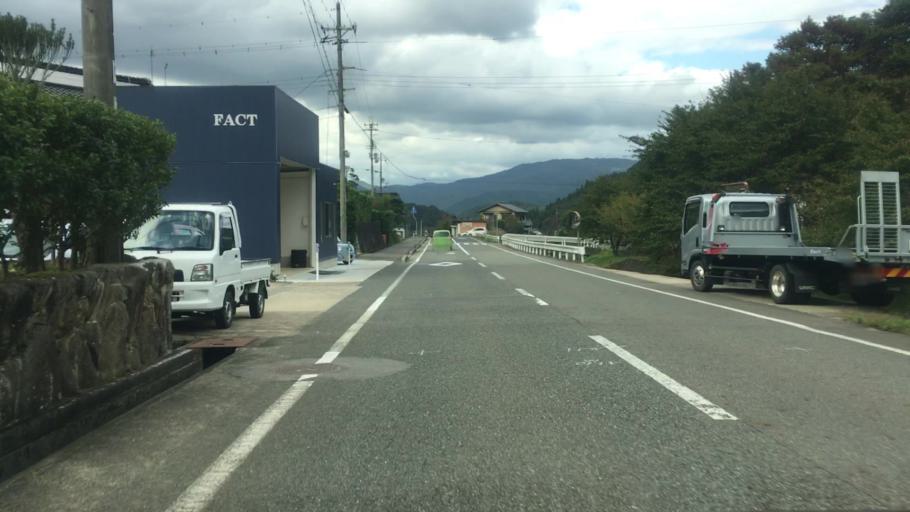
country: JP
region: Hyogo
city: Toyooka
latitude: 35.4361
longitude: 134.7346
